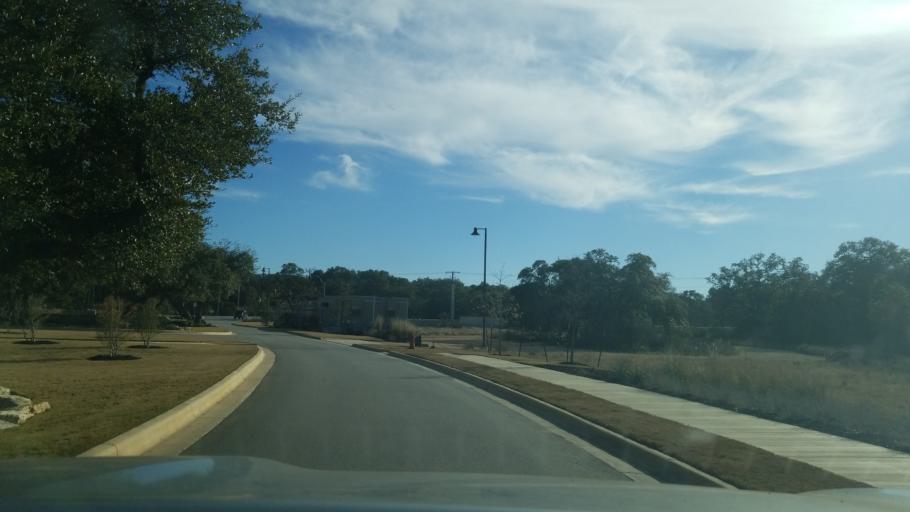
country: US
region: Texas
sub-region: Comal County
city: Canyon Lake
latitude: 29.7751
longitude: -98.2894
